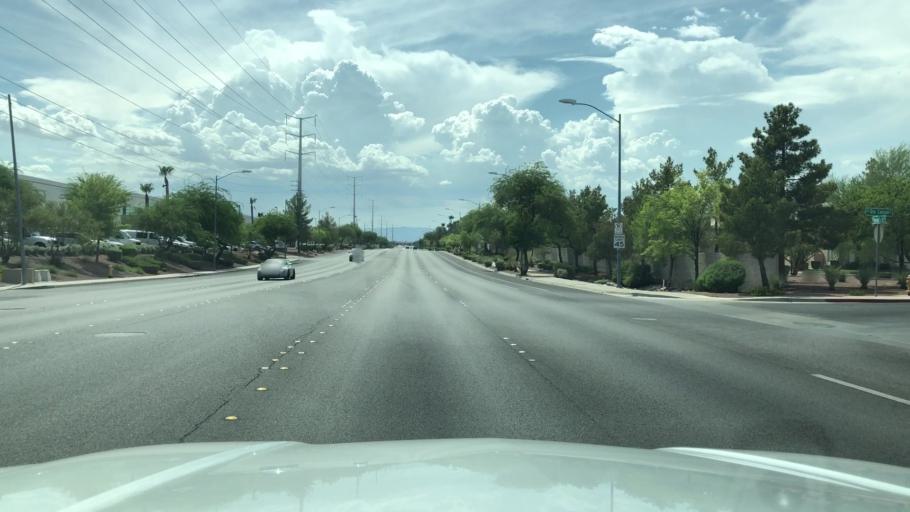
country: US
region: Nevada
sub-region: Clark County
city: Henderson
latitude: 36.0419
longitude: -115.0321
